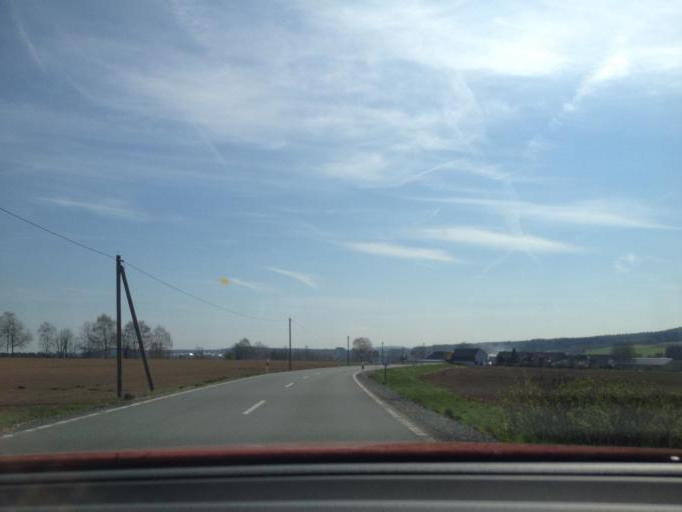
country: DE
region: Bavaria
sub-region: Upper Franconia
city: Zell im Fichtelgebirge
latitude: 50.0958
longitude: 11.8398
